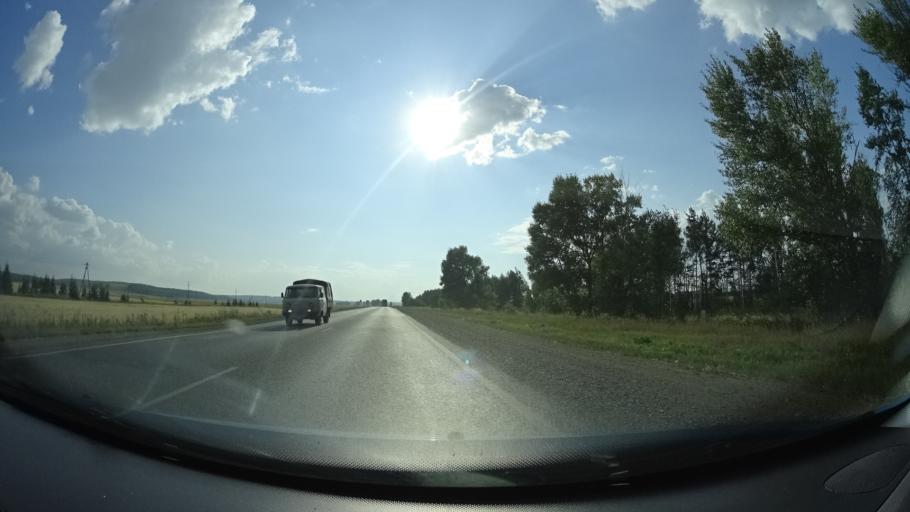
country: RU
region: Tatarstan
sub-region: Bavlinskiy Rayon
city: Bavly
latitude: 54.4768
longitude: 53.3349
